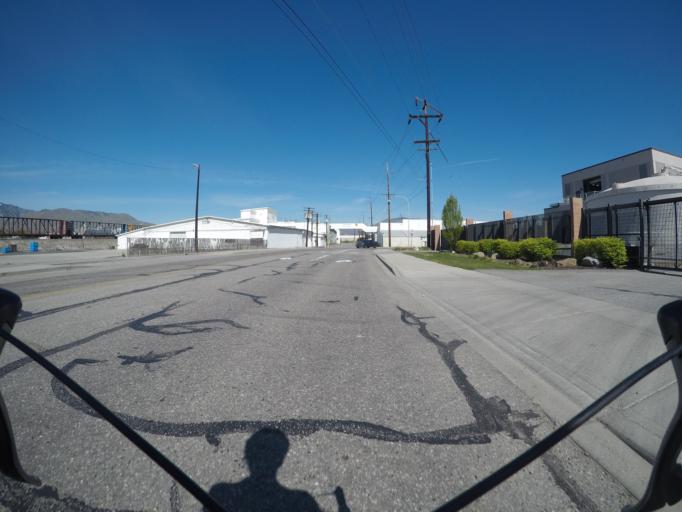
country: US
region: Washington
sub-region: Chelan County
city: Wenatchee
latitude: 47.4290
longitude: -120.3111
